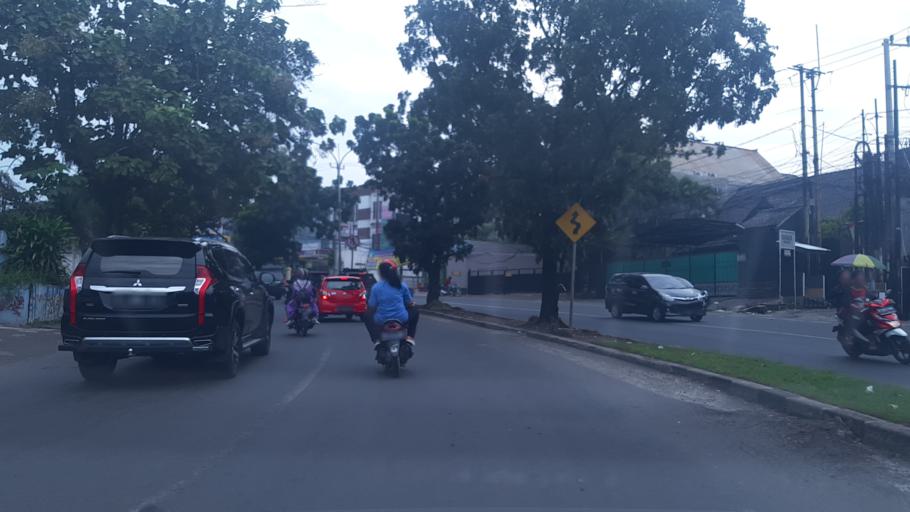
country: ID
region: West Java
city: Cibinong
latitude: -6.4800
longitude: 106.8661
